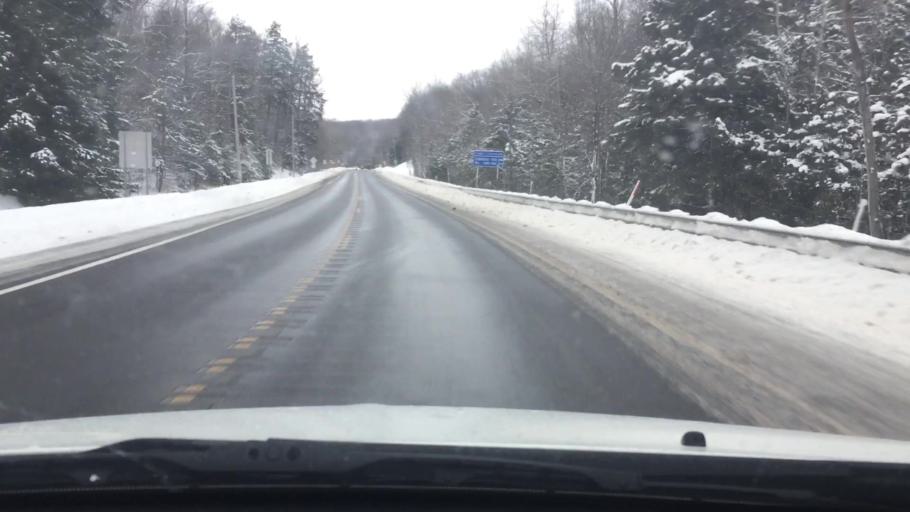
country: US
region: Michigan
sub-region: Charlevoix County
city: East Jordan
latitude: 45.1163
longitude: -85.0603
